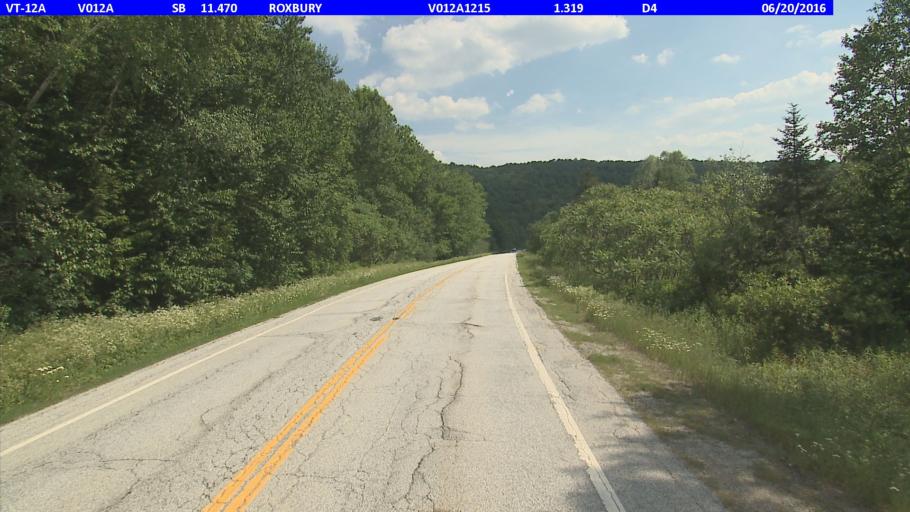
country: US
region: Vermont
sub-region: Washington County
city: Northfield
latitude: 44.0477
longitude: -72.7430
